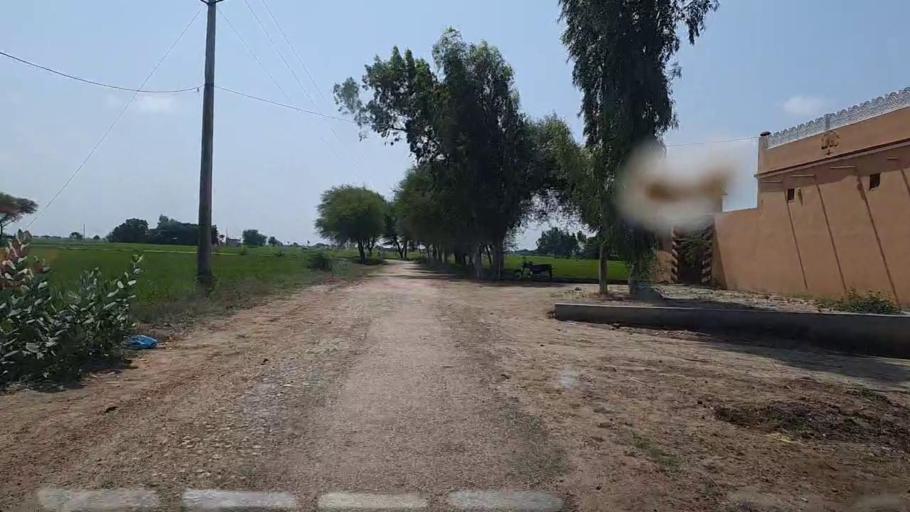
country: PK
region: Sindh
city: Kario
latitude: 24.6340
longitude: 68.5402
